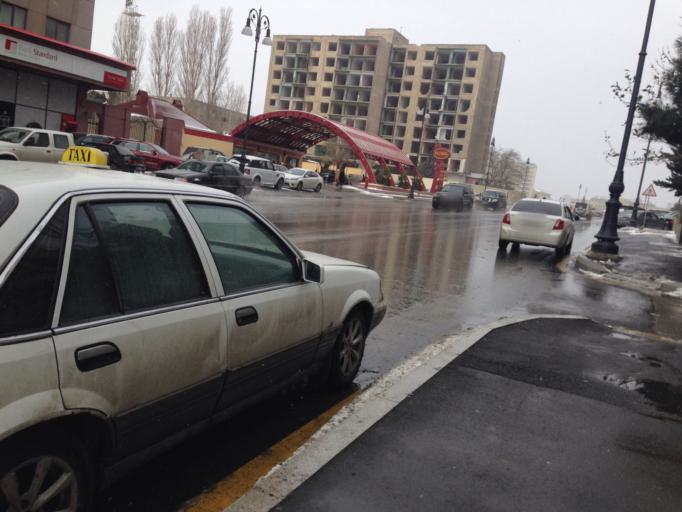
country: AZ
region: Baki
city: Baku
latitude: 40.4000
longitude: 49.8587
